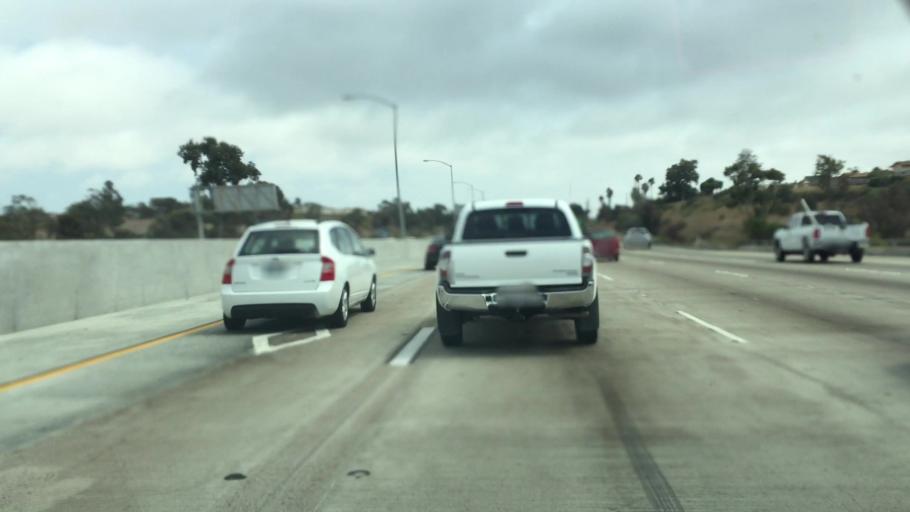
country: US
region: California
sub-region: San Diego County
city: Bonita
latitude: 32.6296
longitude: -117.0439
